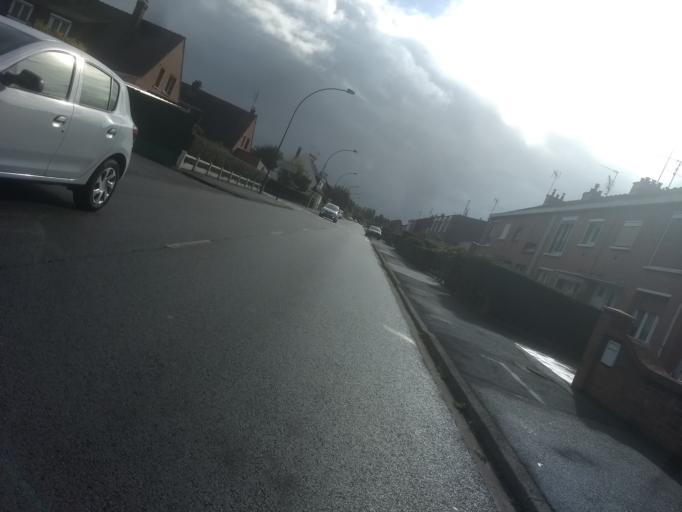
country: FR
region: Nord-Pas-de-Calais
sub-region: Departement du Pas-de-Calais
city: Achicourt
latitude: 50.2707
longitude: 2.7705
